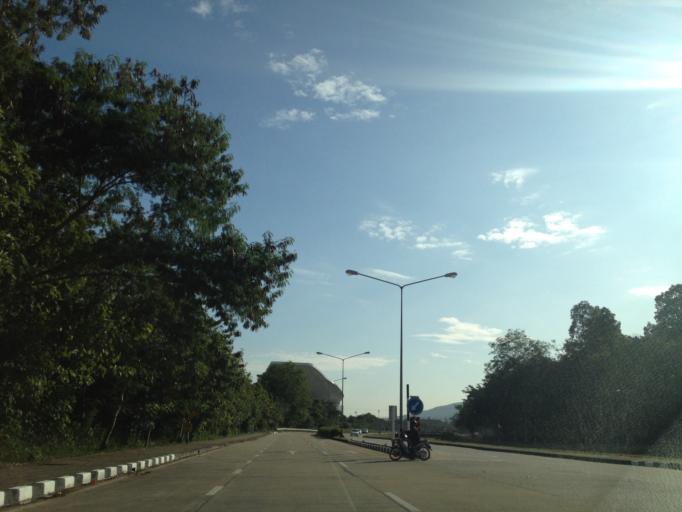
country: TH
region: Chiang Mai
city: Chiang Mai
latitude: 18.8543
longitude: 98.9623
